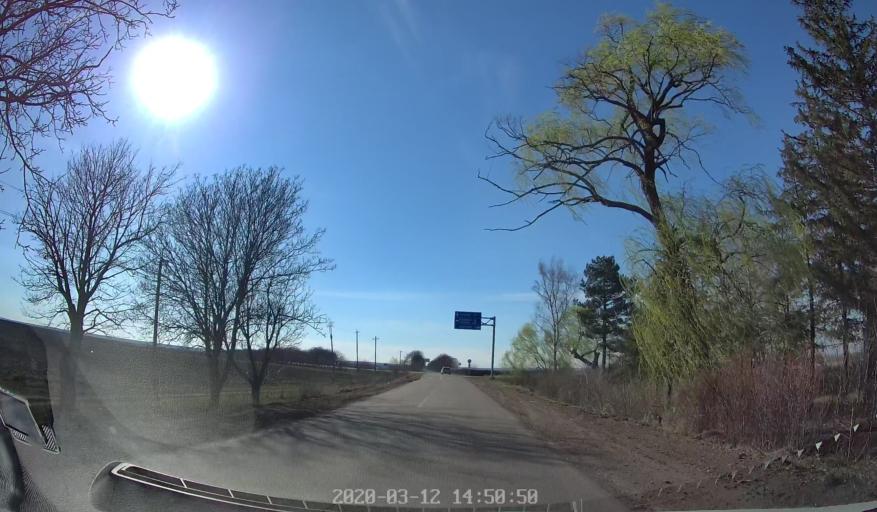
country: MD
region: Criuleni
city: Criuleni
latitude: 47.2228
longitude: 29.1228
